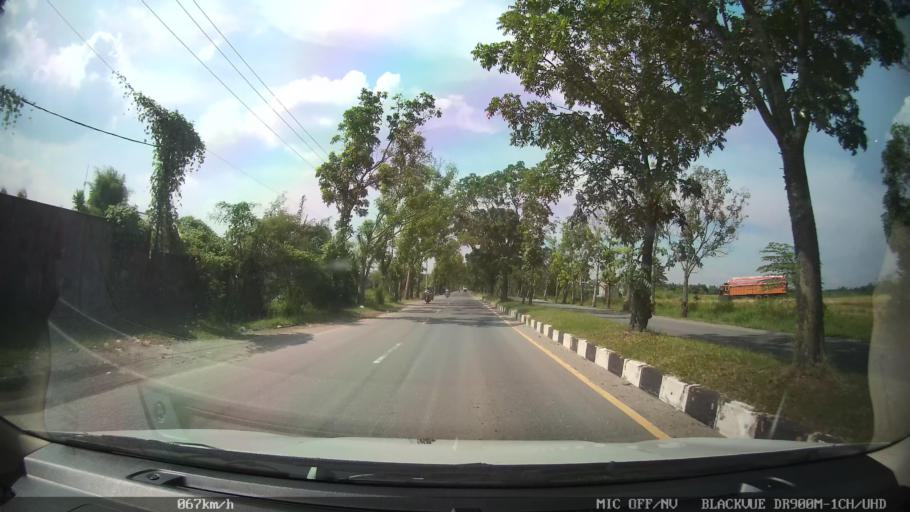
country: ID
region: North Sumatra
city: Binjai
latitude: 3.6263
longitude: 98.5349
